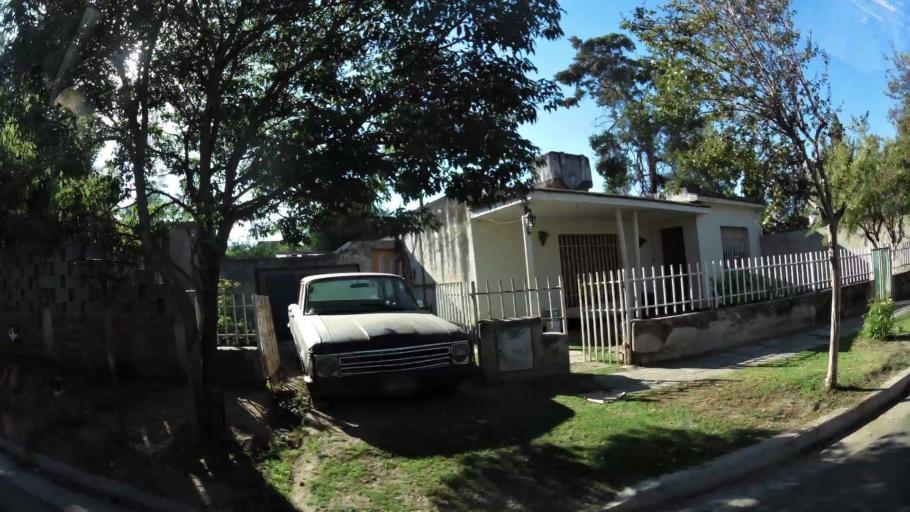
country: AR
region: Cordoba
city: Villa Allende
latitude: -31.3287
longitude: -64.2604
